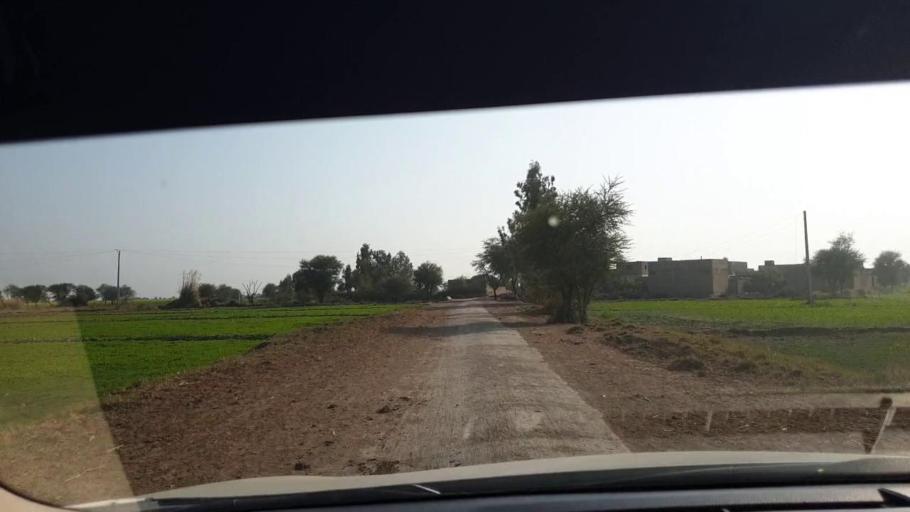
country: PK
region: Sindh
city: Berani
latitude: 25.8128
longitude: 68.7761
